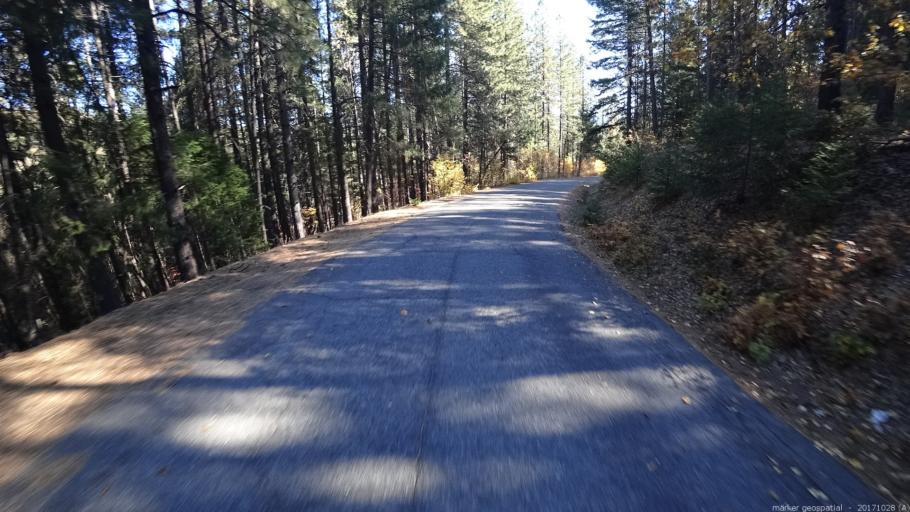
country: US
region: California
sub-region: Trinity County
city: Lewiston
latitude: 40.8109
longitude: -122.6270
